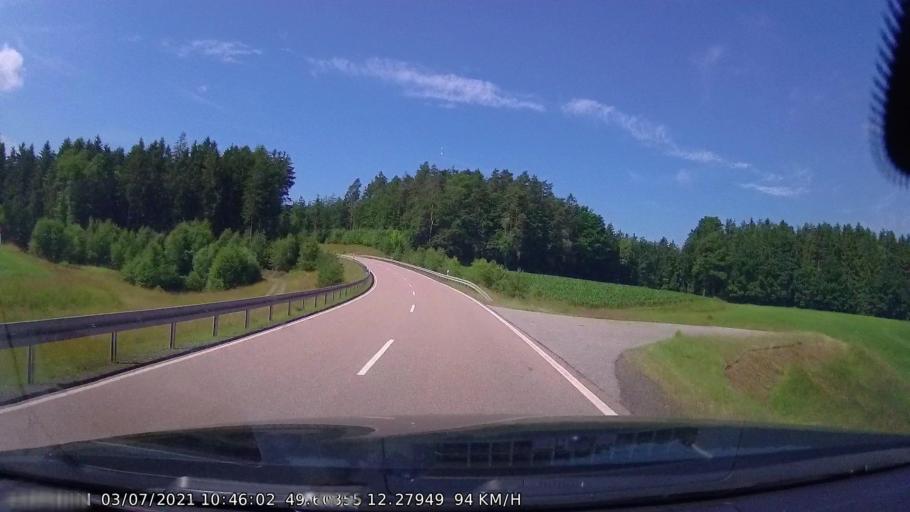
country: DE
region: Bavaria
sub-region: Upper Palatinate
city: Leuchtenberg
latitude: 49.6034
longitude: 12.2790
